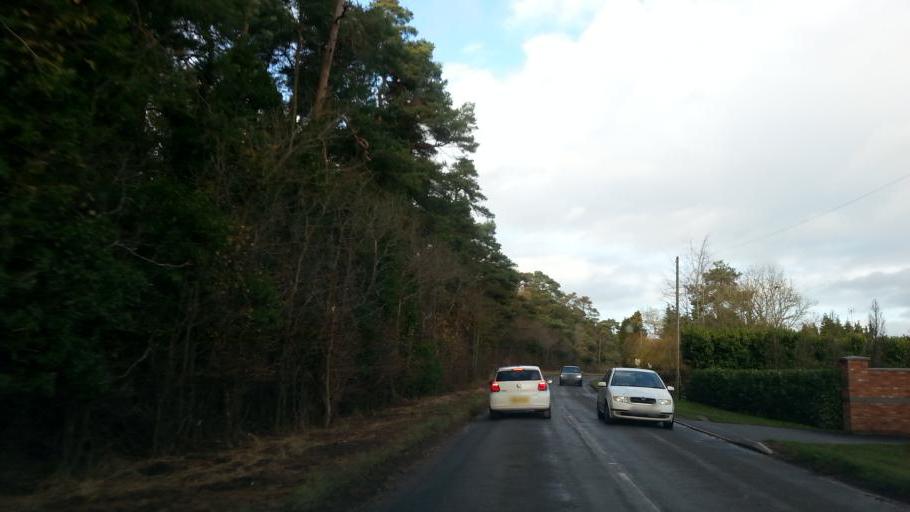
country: GB
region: England
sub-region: Oxfordshire
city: Stanford in the Vale
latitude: 51.6566
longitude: -1.4997
